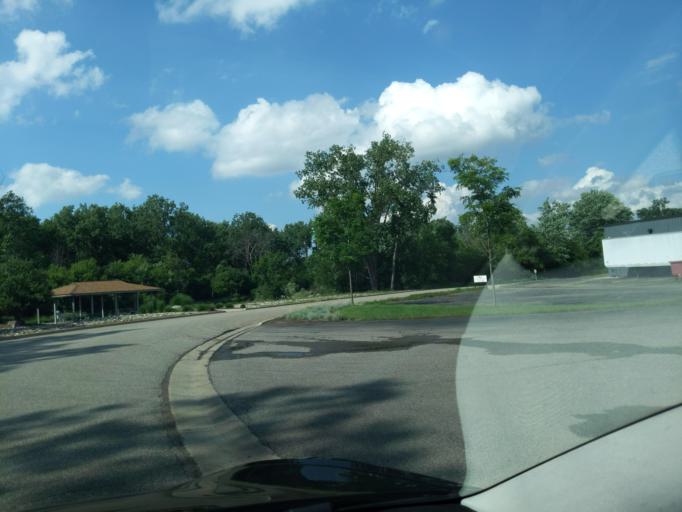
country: US
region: Michigan
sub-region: Jackson County
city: Jackson
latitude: 42.2260
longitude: -84.3703
